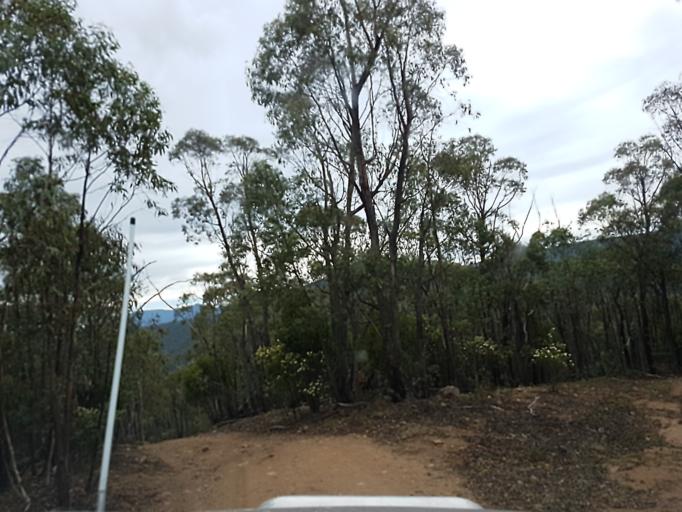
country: AU
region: New South Wales
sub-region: Snowy River
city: Jindabyne
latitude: -36.8739
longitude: 148.3345
